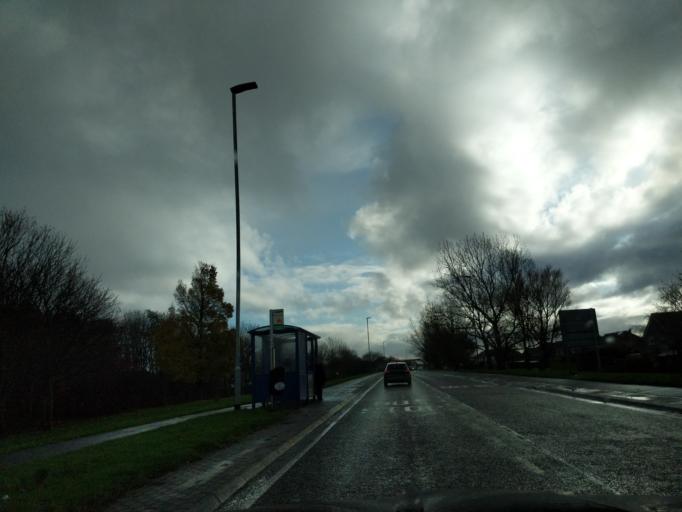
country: GB
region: England
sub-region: Northumberland
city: Blyth
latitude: 55.1180
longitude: -1.5104
